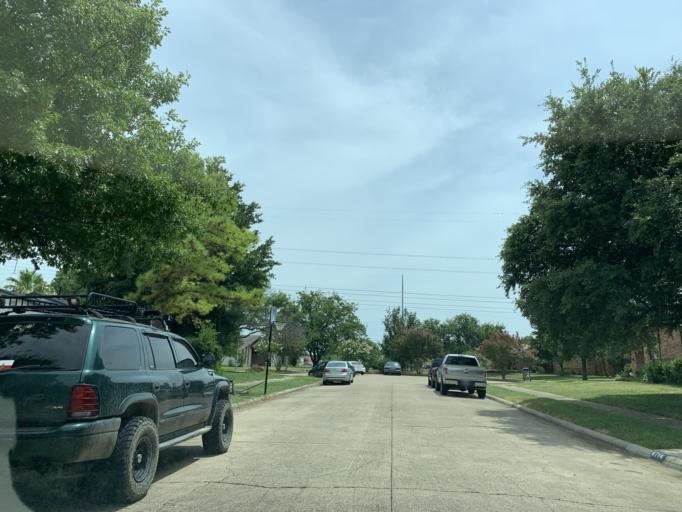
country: US
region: Texas
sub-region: Dallas County
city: Grand Prairie
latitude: 32.6571
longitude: -97.0324
